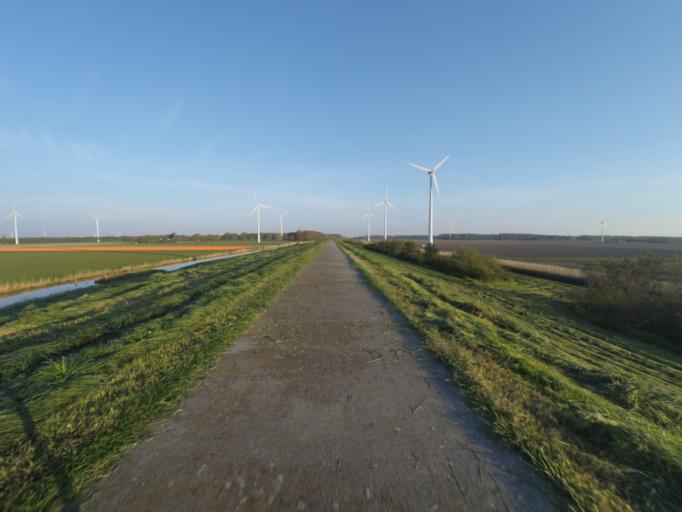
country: NL
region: Flevoland
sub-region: Gemeente Zeewolde
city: Zeewolde
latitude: 52.3949
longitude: 5.5151
